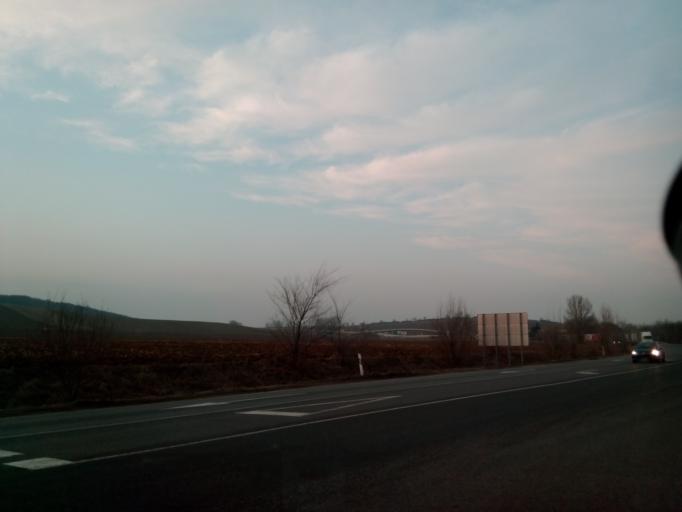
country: HU
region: Borsod-Abauj-Zemplen
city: Gonc
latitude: 48.5266
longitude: 21.2536
